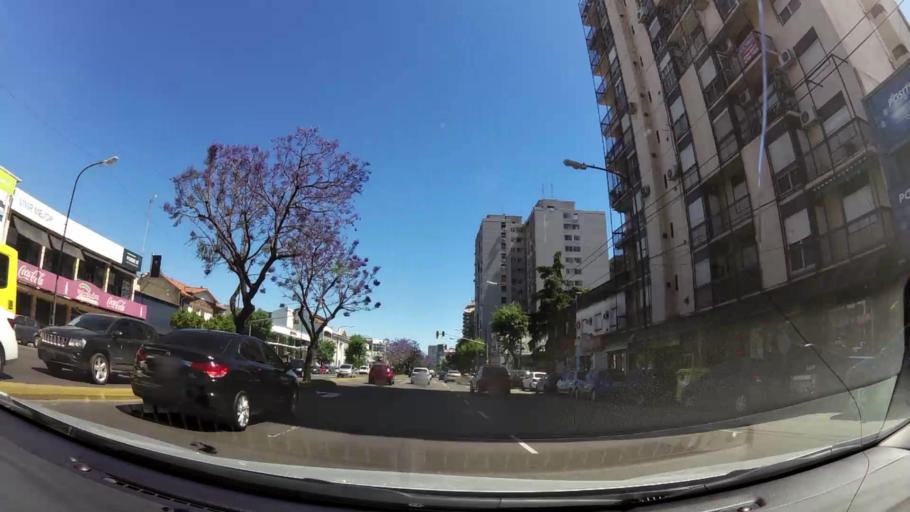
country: AR
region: Buenos Aires
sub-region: Partido de San Isidro
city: San Isidro
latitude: -34.4832
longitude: -58.5045
